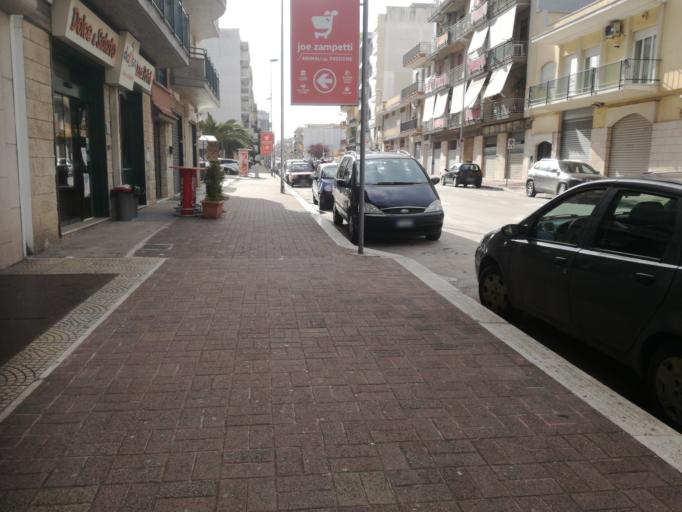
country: IT
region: Apulia
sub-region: Provincia di Barletta - Andria - Trani
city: Andria
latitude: 41.2370
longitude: 16.2946
